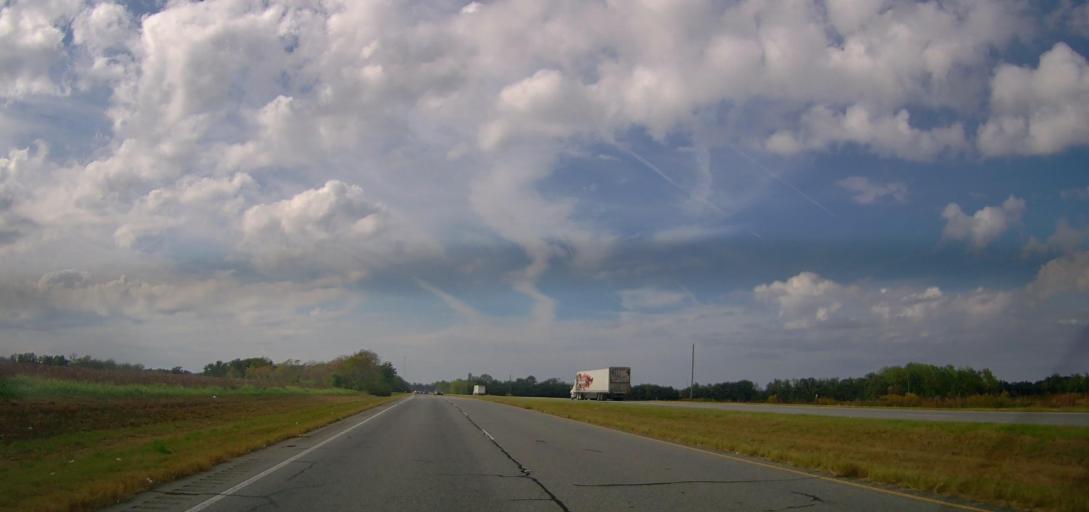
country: US
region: Georgia
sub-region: Mitchell County
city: Pelham
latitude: 31.1112
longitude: -84.1227
